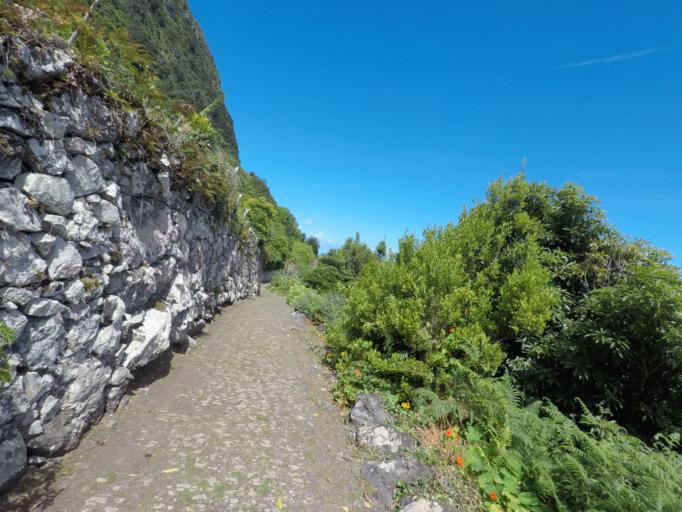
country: PT
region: Madeira
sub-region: Santana
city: Santana
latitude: 32.8251
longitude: -16.9620
